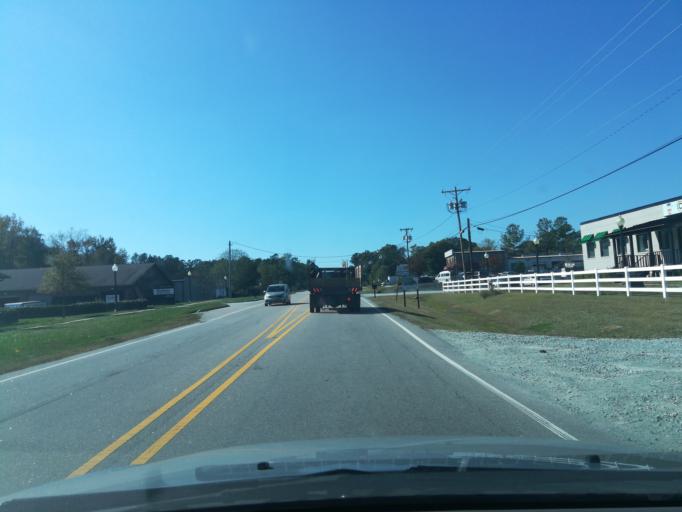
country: US
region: North Carolina
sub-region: Durham County
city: Durham
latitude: 36.0334
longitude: -78.9739
